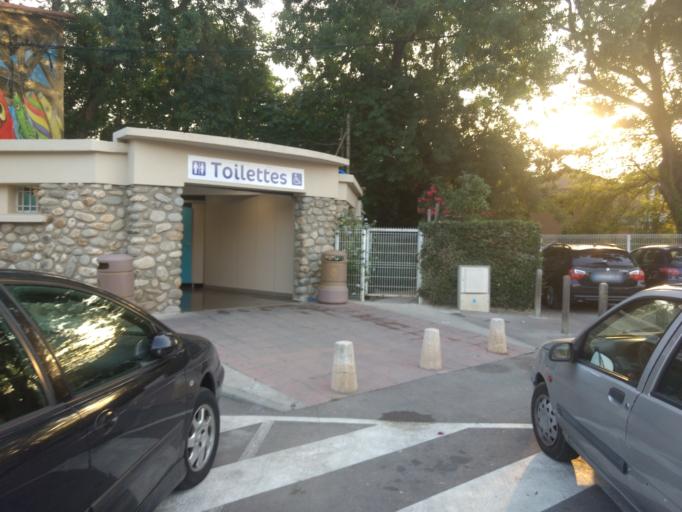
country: FR
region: Languedoc-Roussillon
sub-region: Departement des Pyrenees-Orientales
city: Argelers
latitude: 42.5503
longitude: 3.0467
